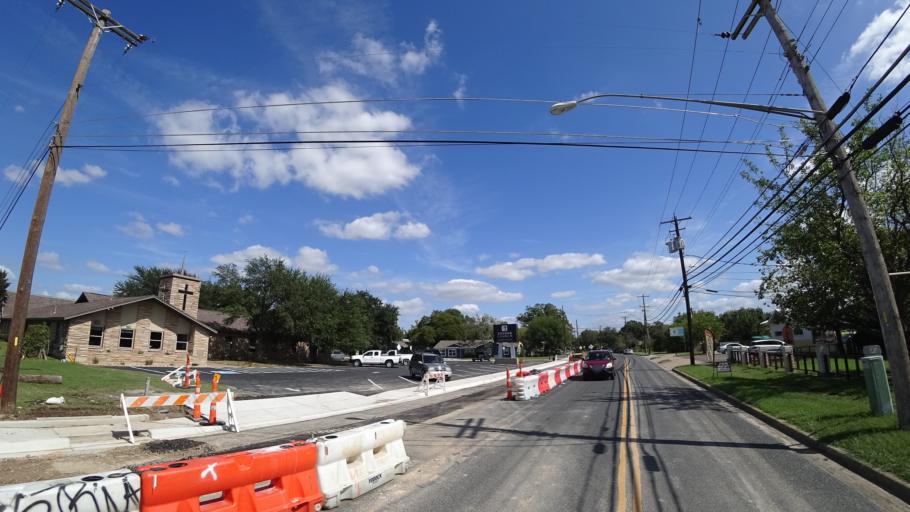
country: US
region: Texas
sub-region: Travis County
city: Austin
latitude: 30.3442
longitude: -97.7348
